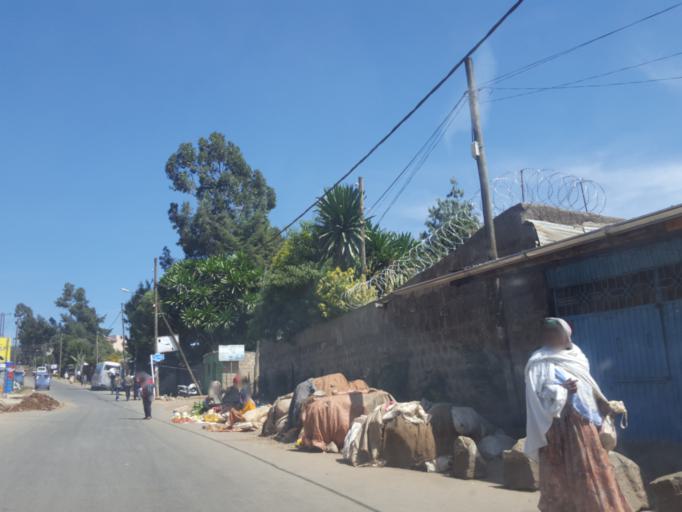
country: ET
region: Adis Abeba
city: Addis Ababa
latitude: 9.0588
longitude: 38.7292
